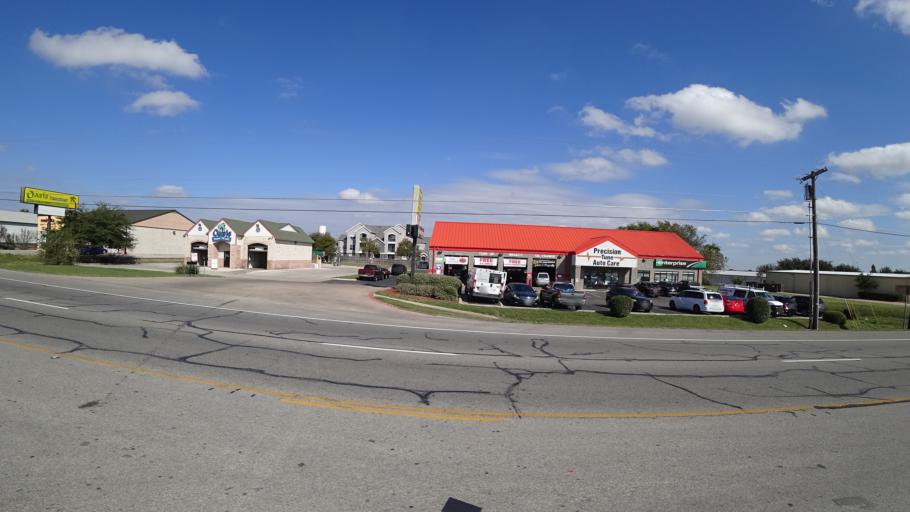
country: US
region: Texas
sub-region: Travis County
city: Windemere
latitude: 30.4464
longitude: -97.6511
